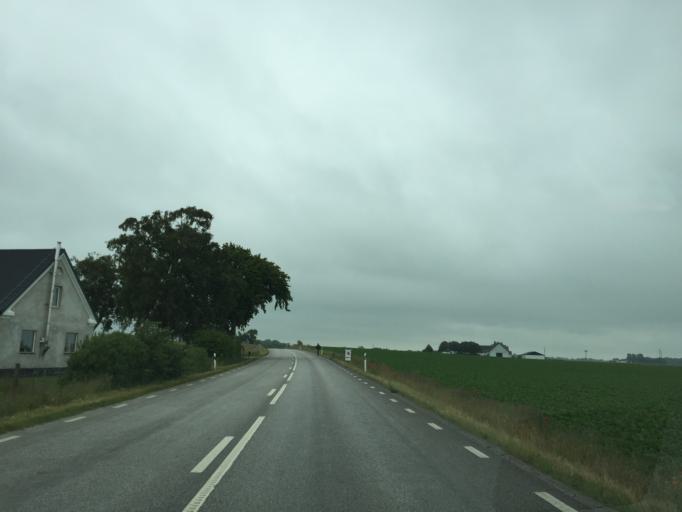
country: SE
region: Skane
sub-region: Ystads Kommun
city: Kopingebro
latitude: 55.4406
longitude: 13.9966
